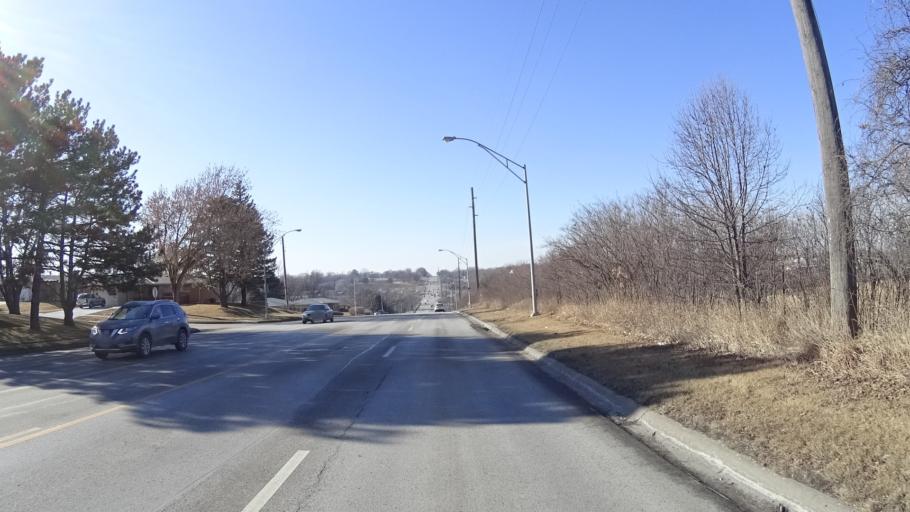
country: US
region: Nebraska
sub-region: Douglas County
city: Ralston
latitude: 41.3068
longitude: -96.0434
